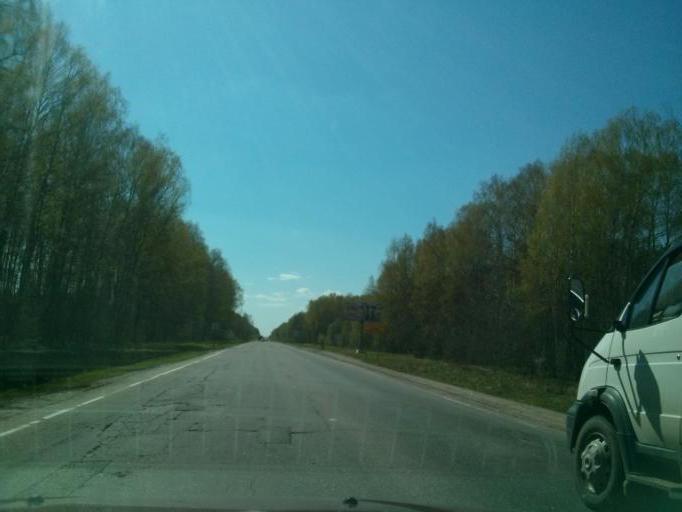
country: RU
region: Nizjnij Novgorod
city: Vorsma
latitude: 56.0118
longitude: 43.3403
